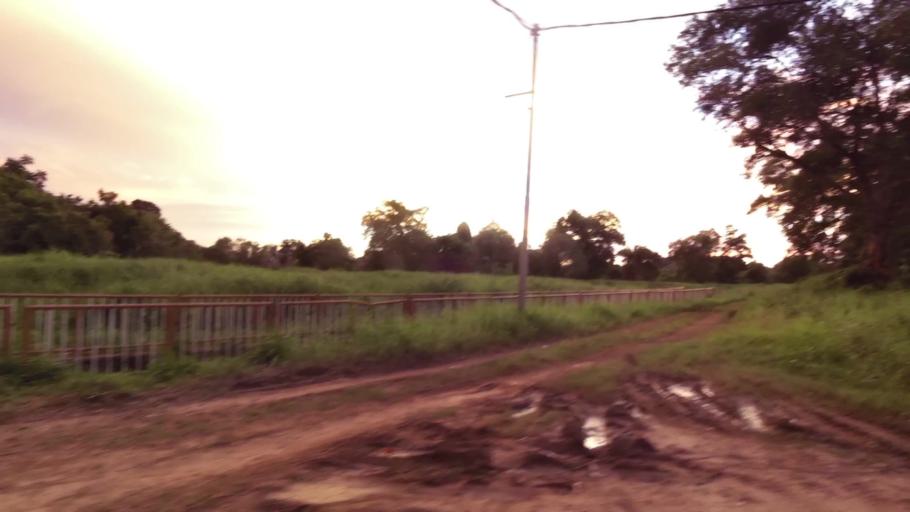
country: BN
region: Brunei and Muara
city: Bandar Seri Begawan
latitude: 4.9998
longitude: 114.9964
